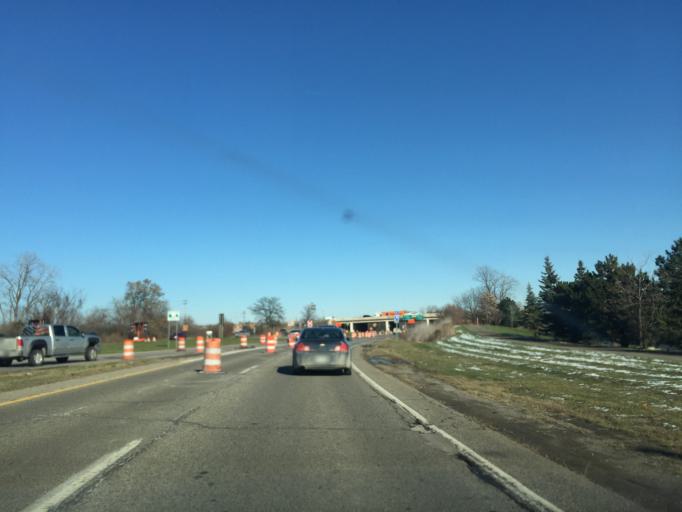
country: US
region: Michigan
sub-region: Oakland County
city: Auburn Hills
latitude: 42.6814
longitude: -83.2455
